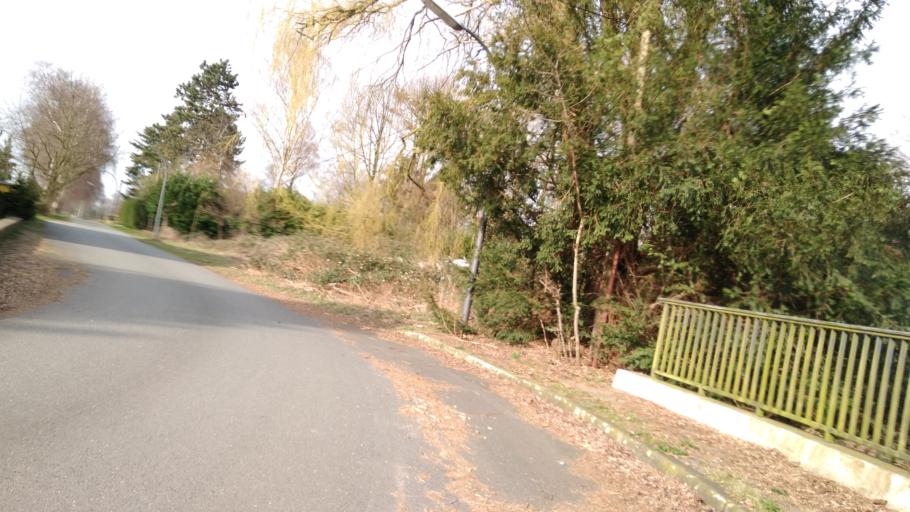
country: DE
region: North Rhine-Westphalia
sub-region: Regierungsbezirk Munster
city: Recklinghausen
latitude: 51.6212
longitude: 7.1654
